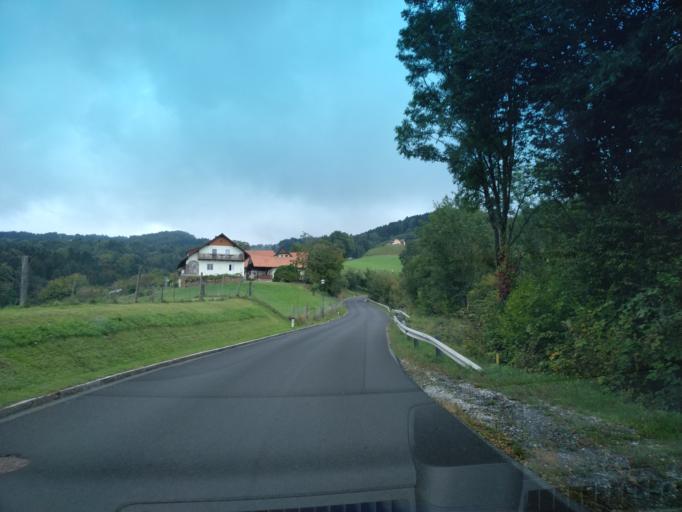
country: AT
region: Styria
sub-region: Politischer Bezirk Deutschlandsberg
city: Deutschlandsberg
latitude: 46.8253
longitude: 15.2003
